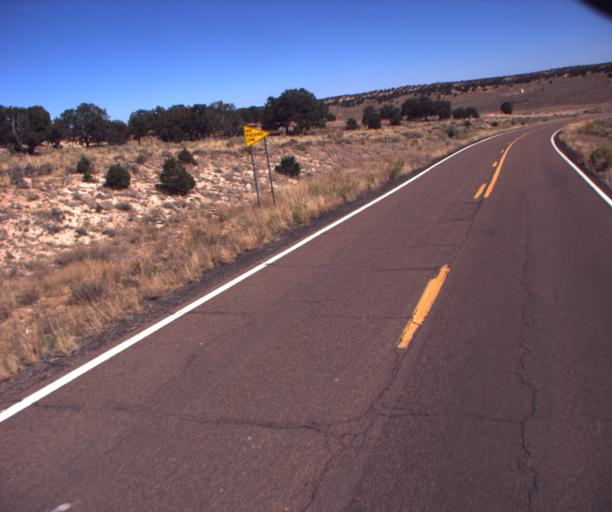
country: US
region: Arizona
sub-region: Navajo County
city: First Mesa
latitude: 35.7664
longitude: -109.9894
